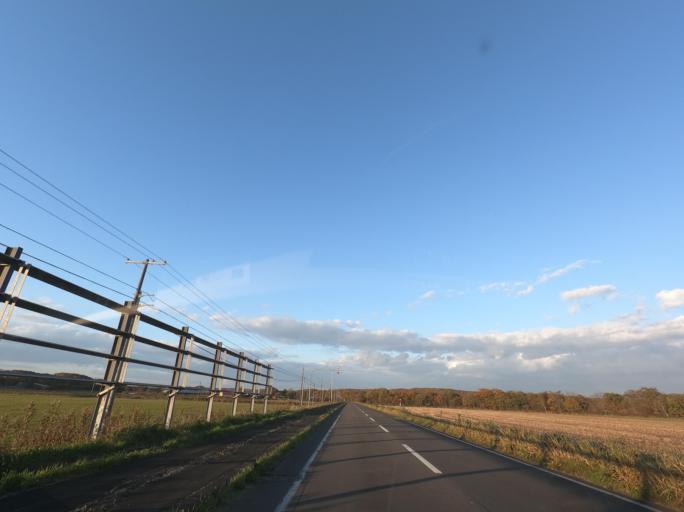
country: JP
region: Hokkaido
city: Kushiro
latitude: 43.2123
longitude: 144.4297
